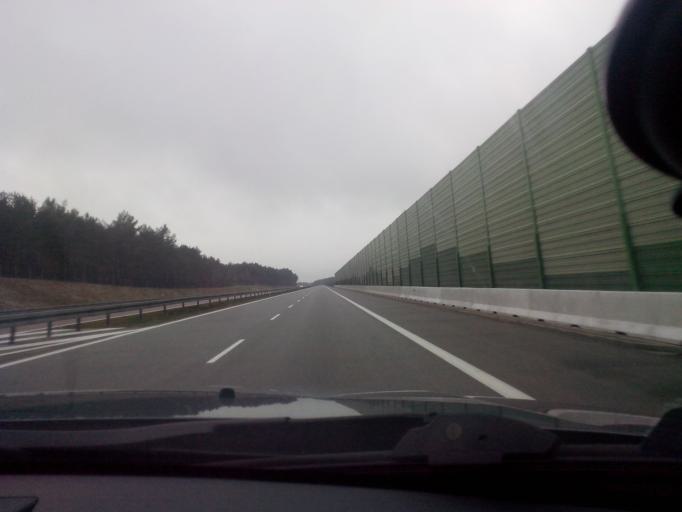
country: PL
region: Lubusz
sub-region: Powiat slubicki
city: Rzepin
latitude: 52.3319
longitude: 14.8218
